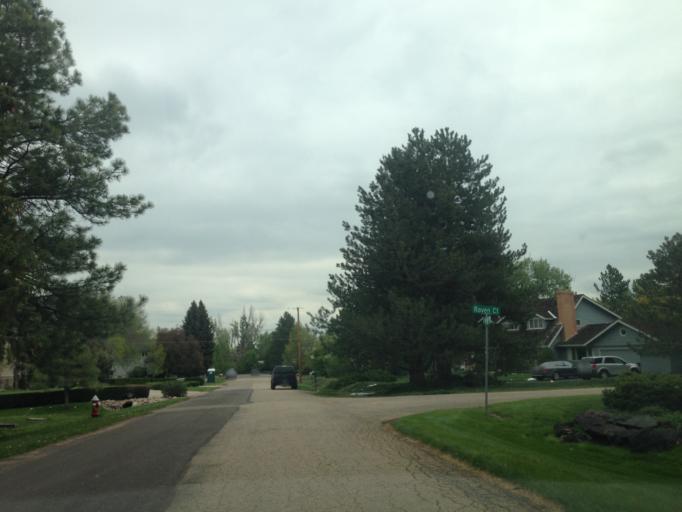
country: US
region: Colorado
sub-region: Boulder County
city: Louisville
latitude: 40.0020
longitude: -105.1712
